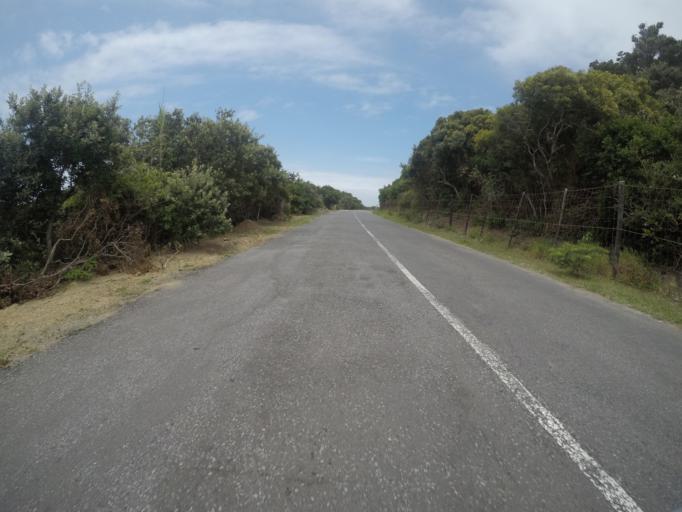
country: ZA
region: Eastern Cape
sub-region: Buffalo City Metropolitan Municipality
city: East London
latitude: -32.9934
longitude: 27.9461
